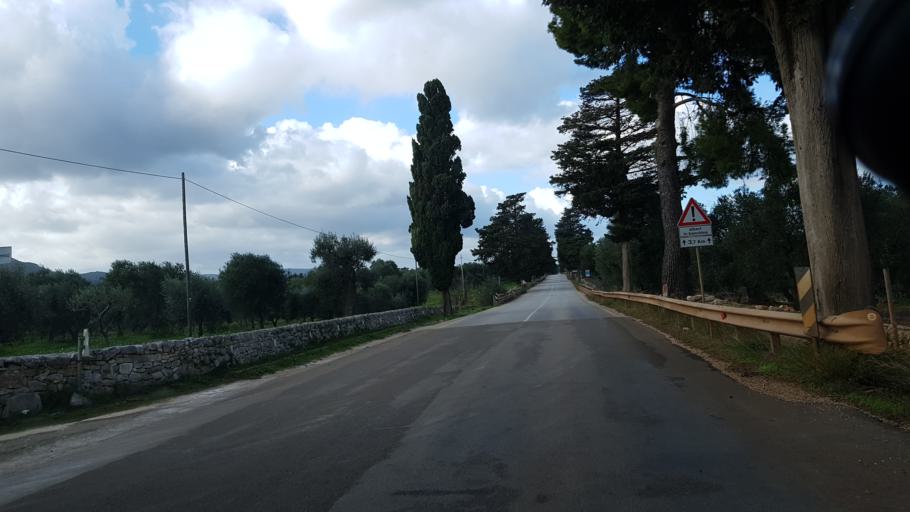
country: IT
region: Apulia
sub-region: Provincia di Brindisi
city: Montalbano
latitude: 40.7631
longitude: 17.5234
